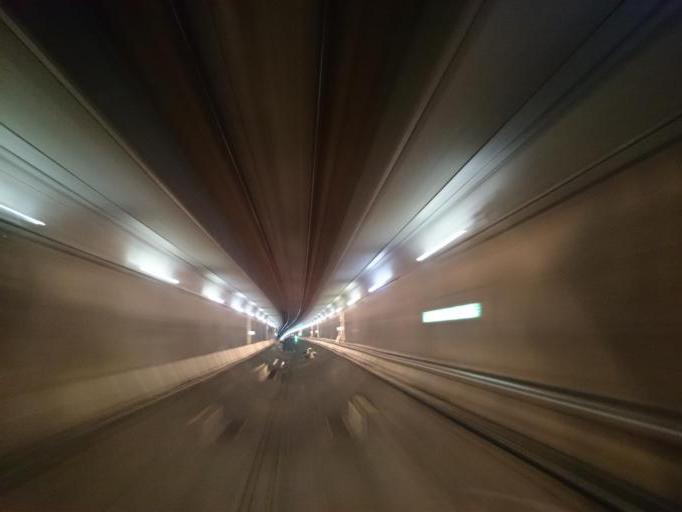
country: SE
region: Skane
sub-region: Malmo
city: Malmoe
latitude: 55.5697
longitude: 12.9864
